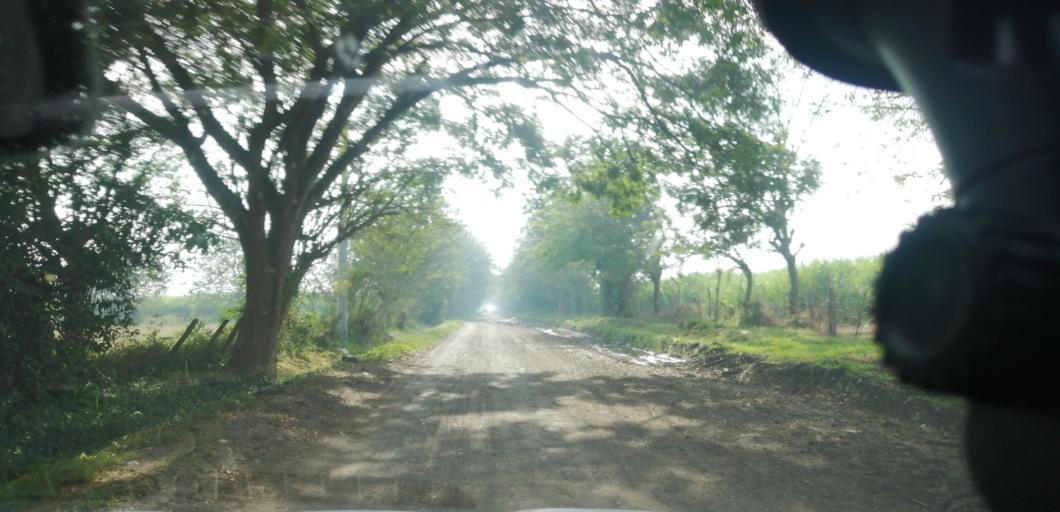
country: CO
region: Valle del Cauca
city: Yumbo
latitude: 3.5827
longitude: -76.4231
